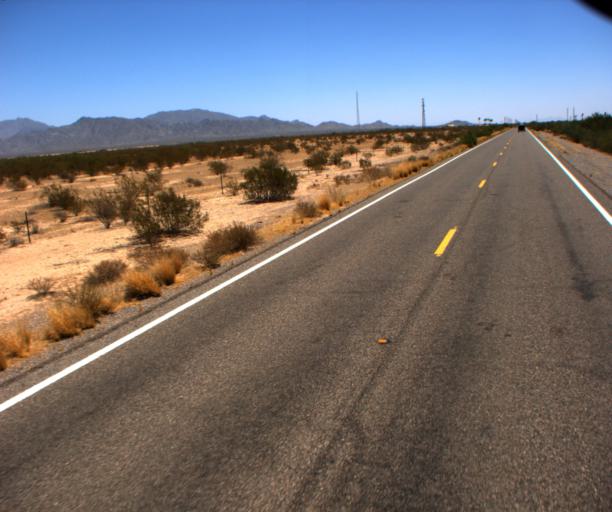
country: US
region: Arizona
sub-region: Pinal County
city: Maricopa
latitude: 33.0526
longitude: -112.2829
